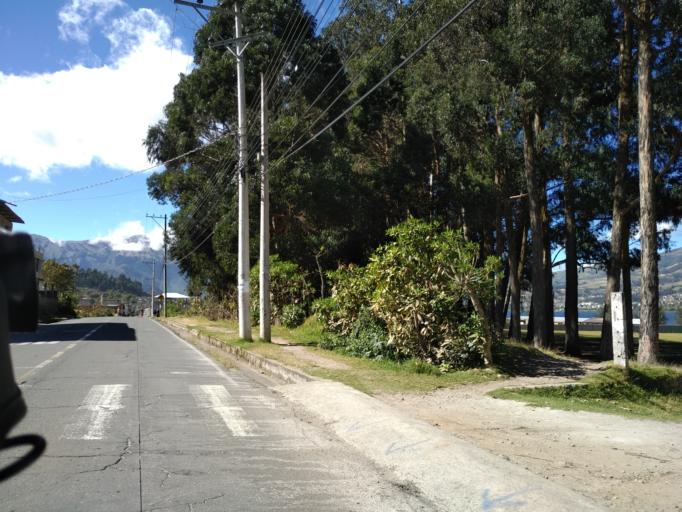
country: EC
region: Imbabura
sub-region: Canton Otavalo
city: Otavalo
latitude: 0.2193
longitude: -78.2190
